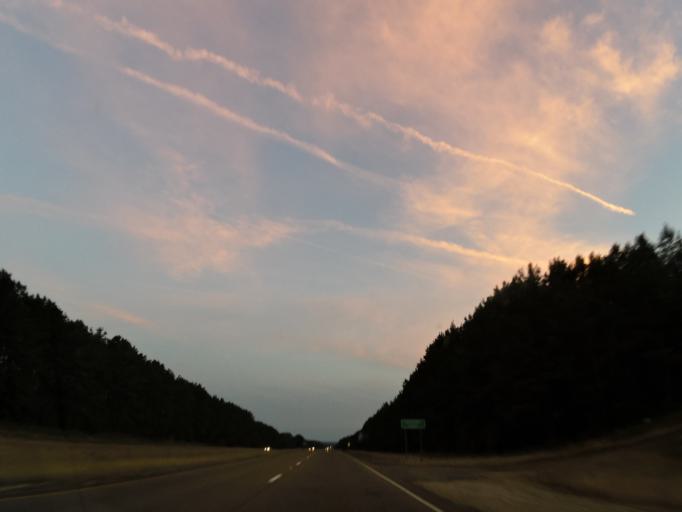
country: US
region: Mississippi
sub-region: Lauderdale County
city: Meridian Station
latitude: 32.5783
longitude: -88.5030
